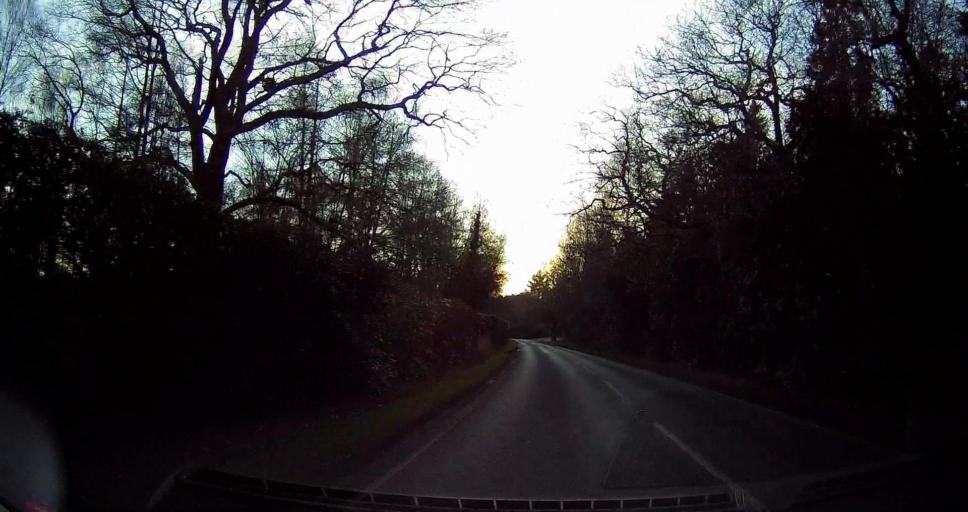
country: GB
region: England
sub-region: West Sussex
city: Maidenbower
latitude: 51.0931
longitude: -0.1259
